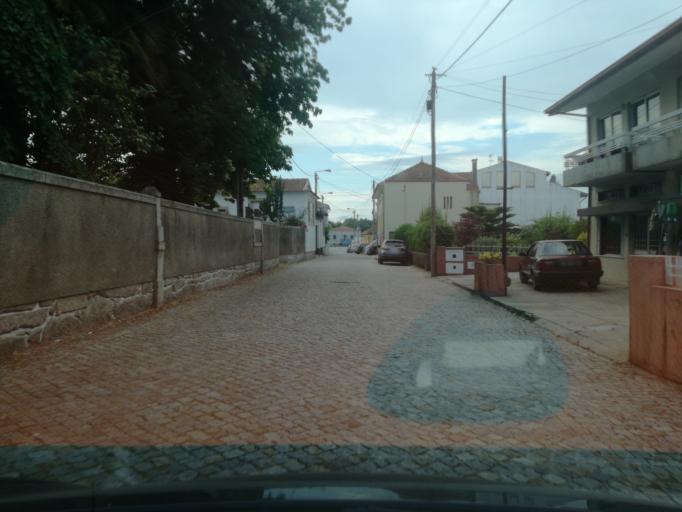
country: PT
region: Porto
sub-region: Maia
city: Maia
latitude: 41.2388
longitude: -8.6056
